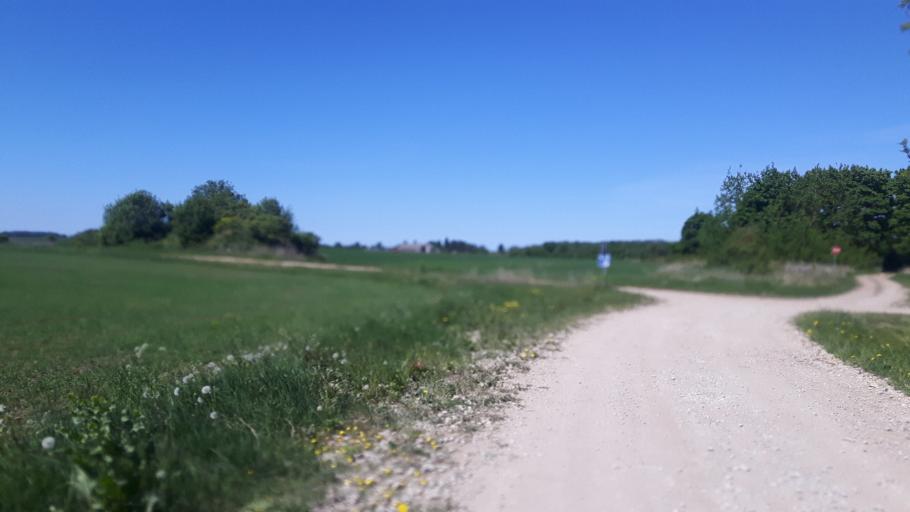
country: EE
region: Ida-Virumaa
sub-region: Toila vald
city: Voka
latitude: 59.4031
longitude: 27.6644
